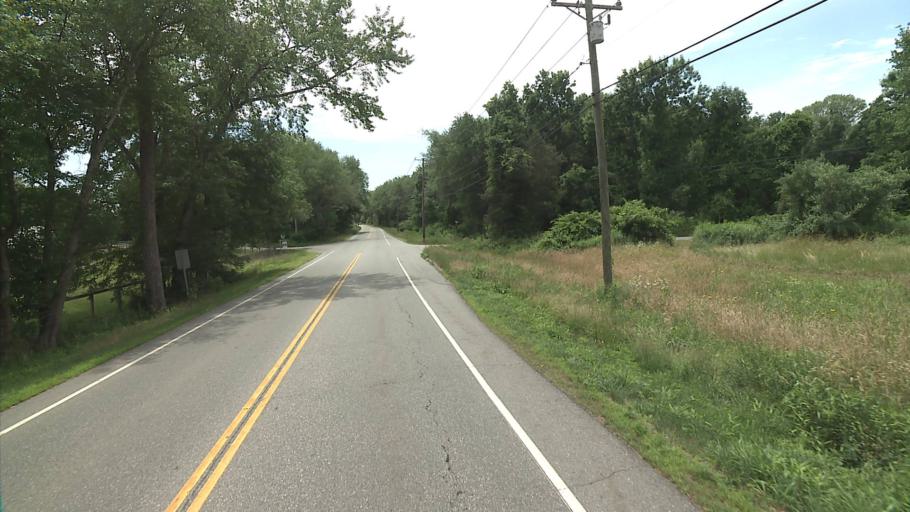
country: US
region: Connecticut
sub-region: New London County
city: Preston City
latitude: 41.5059
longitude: -71.9841
